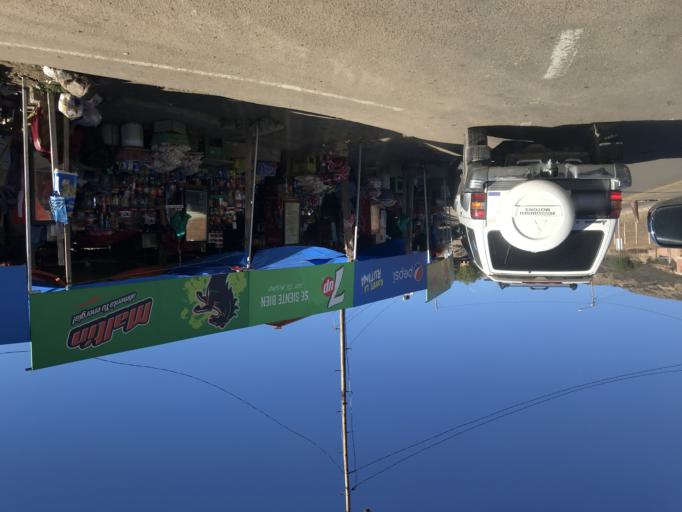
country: BO
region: Chuquisaca
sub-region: Provincia Oropeza
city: Yotala
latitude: -19.1330
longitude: -65.2071
